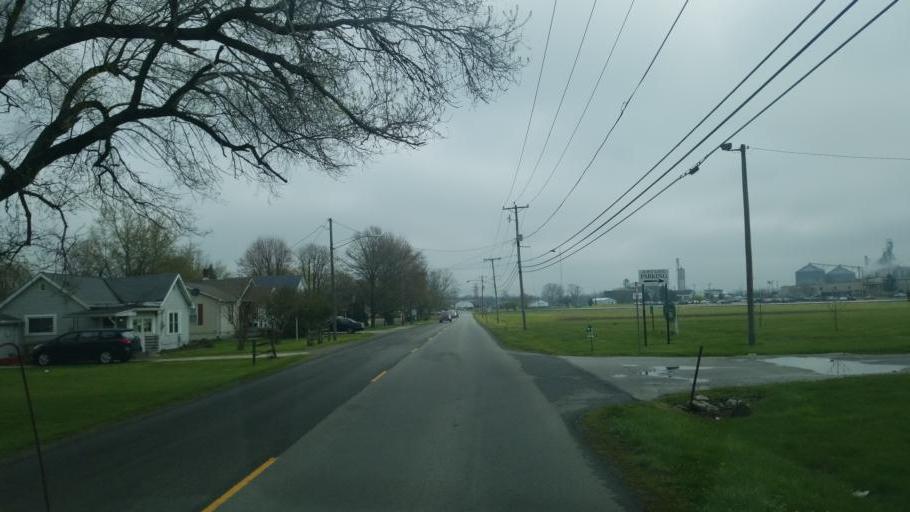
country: US
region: Ohio
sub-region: Hardin County
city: Kenton
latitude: 40.6336
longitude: -83.6075
